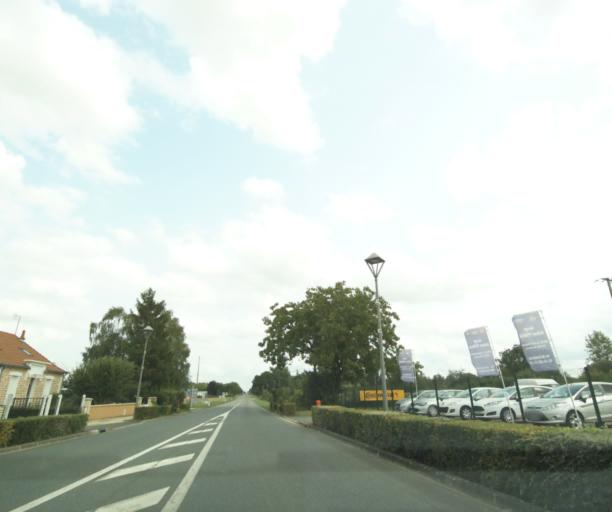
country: FR
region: Centre
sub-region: Departement de l'Indre
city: Buzancais
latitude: 46.8877
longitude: 1.4348
